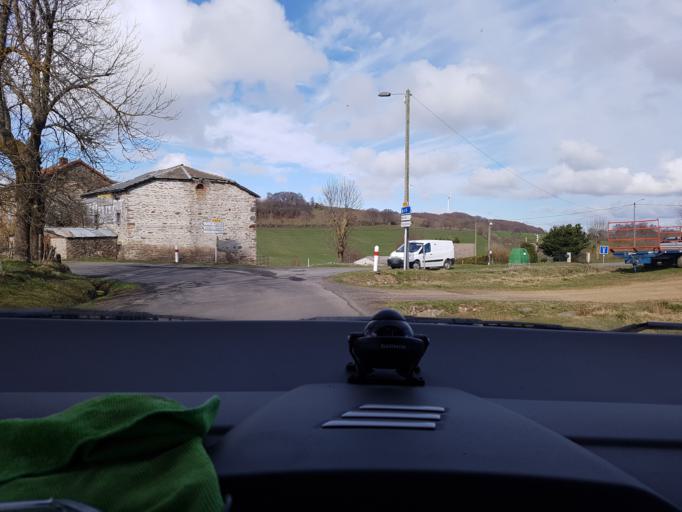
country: FR
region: Auvergne
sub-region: Departement du Cantal
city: Saint-Flour
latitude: 45.1160
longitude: 3.1336
